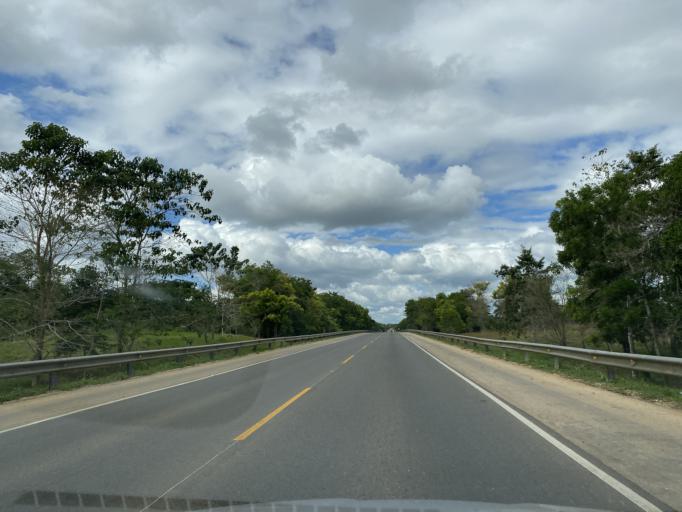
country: DO
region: Santo Domingo
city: Guerra
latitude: 18.5356
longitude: -69.7548
